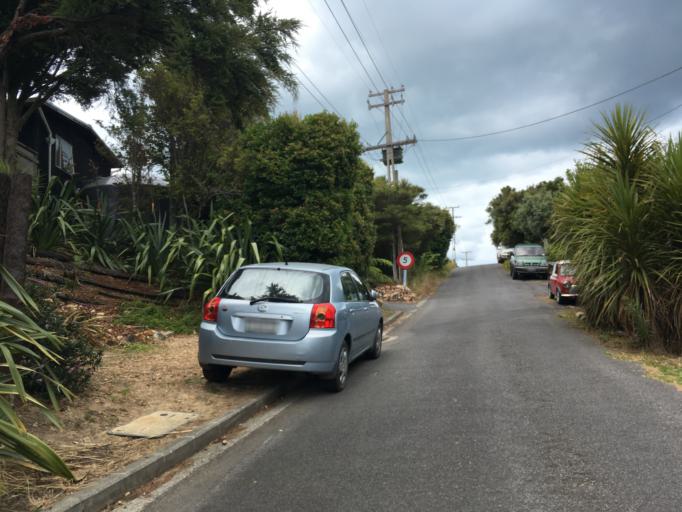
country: NZ
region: Auckland
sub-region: Auckland
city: Pakuranga
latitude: -36.7890
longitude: 175.0208
